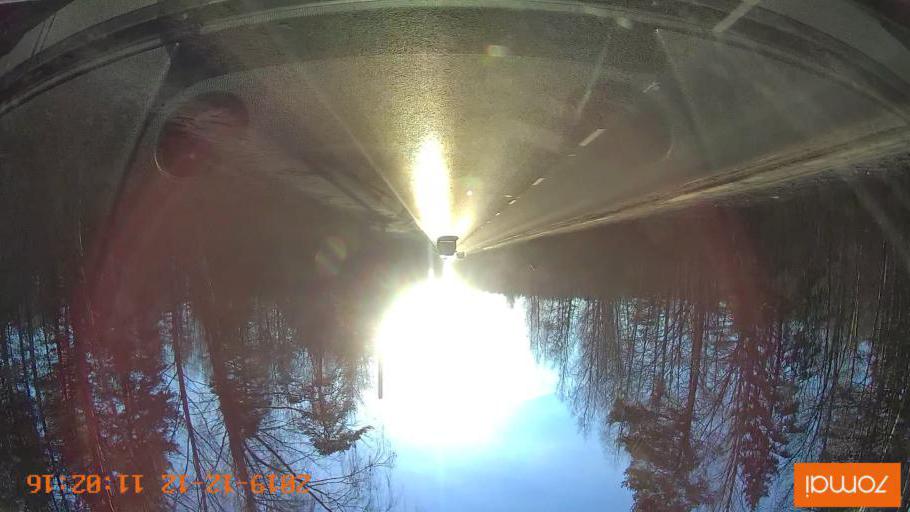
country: RU
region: Ivanovo
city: Kokhma
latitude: 56.9664
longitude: 41.0932
